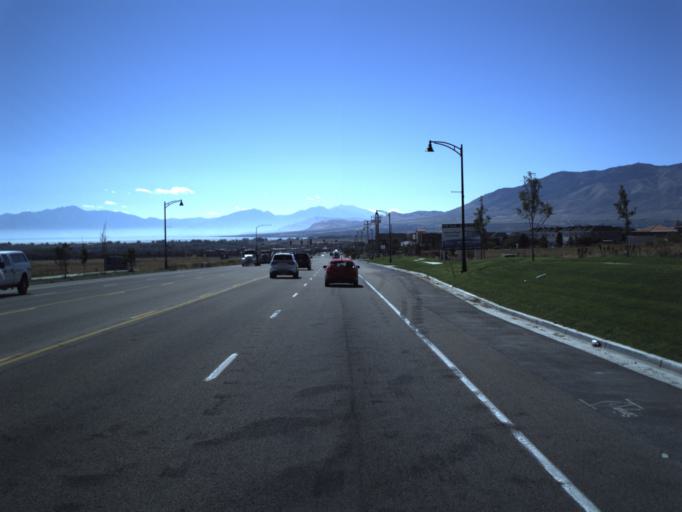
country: US
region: Utah
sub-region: Utah County
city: Saratoga Springs
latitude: 40.4023
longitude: -111.9202
